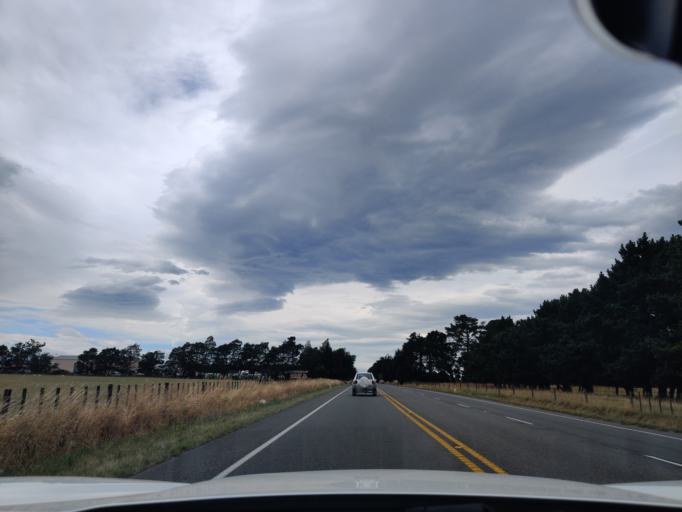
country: NZ
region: Wellington
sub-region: Masterton District
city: Masterton
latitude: -40.9775
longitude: 175.5905
